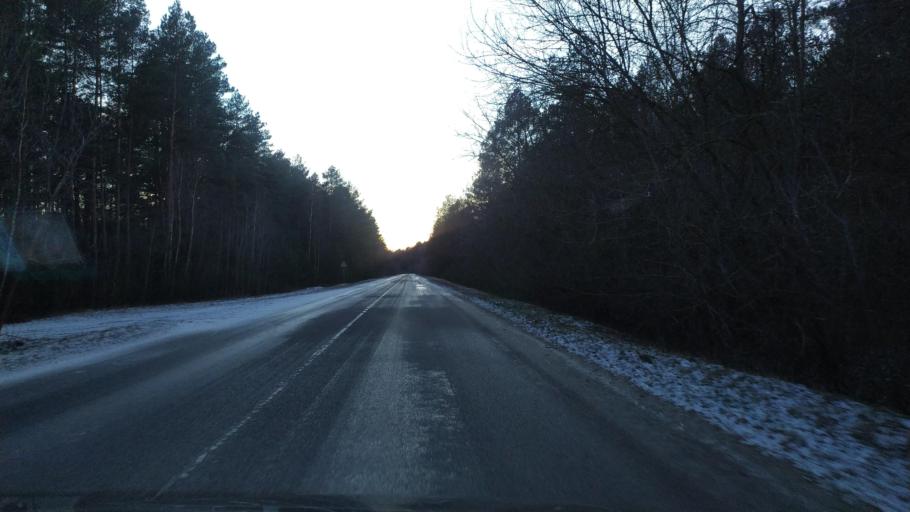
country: BY
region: Brest
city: Pruzhany
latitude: 52.5325
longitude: 24.1913
